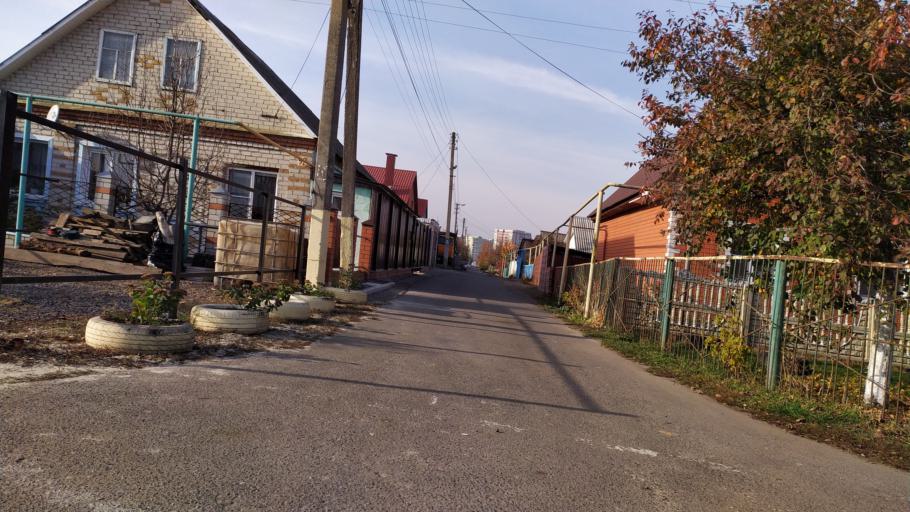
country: RU
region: Kursk
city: Kursk
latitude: 51.6430
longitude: 36.1513
